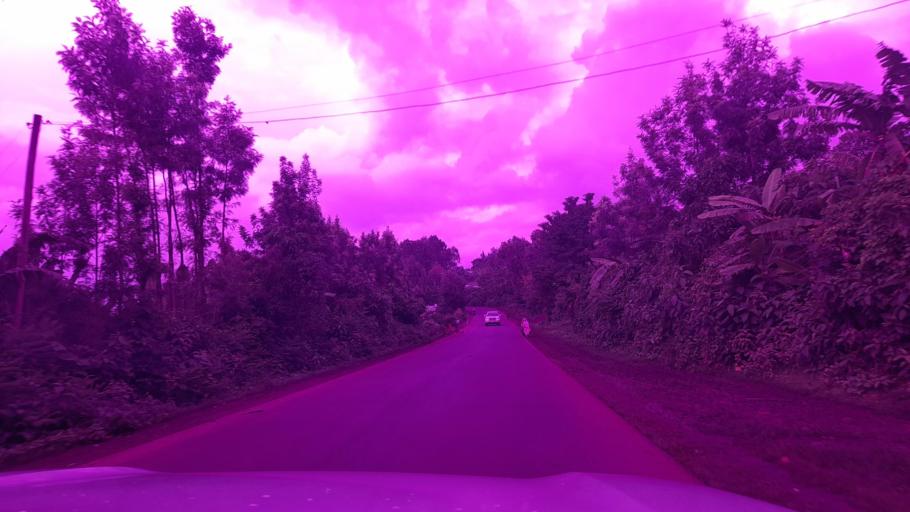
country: ET
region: Oromiya
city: Jima
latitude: 7.9062
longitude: 37.3924
